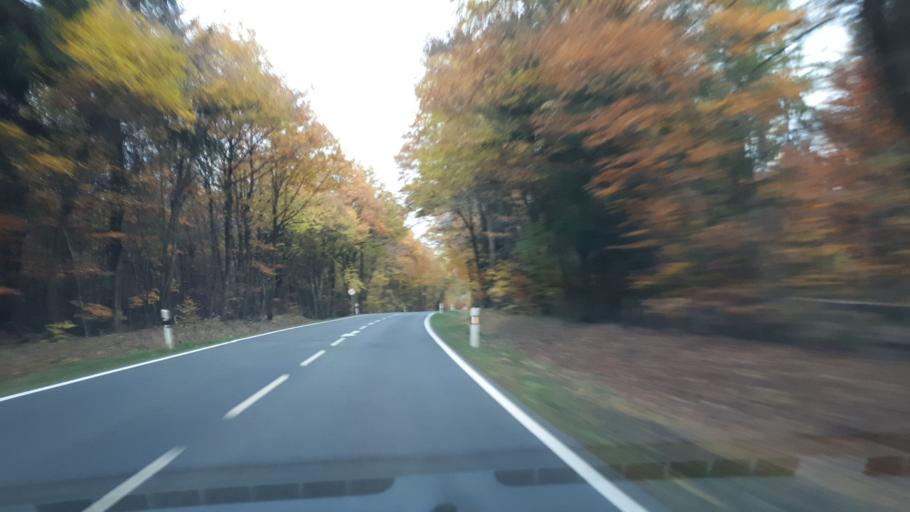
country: DE
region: Rheinland-Pfalz
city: Gillenbeuren
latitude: 50.1557
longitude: 7.0345
